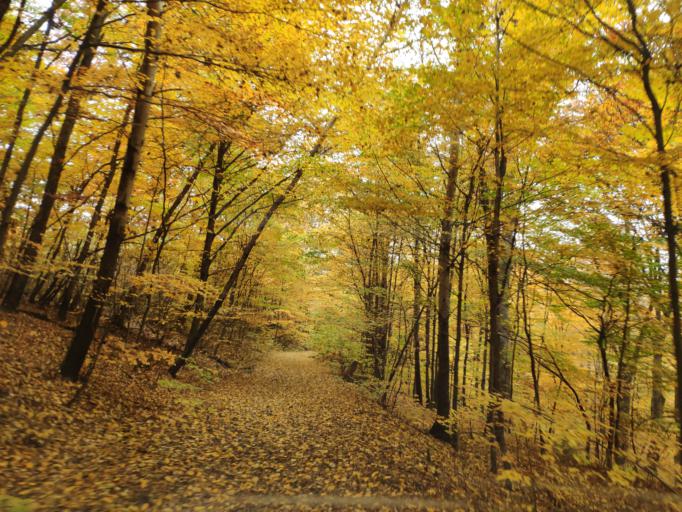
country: SK
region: Kosicky
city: Kosice
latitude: 48.7239
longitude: 21.1100
